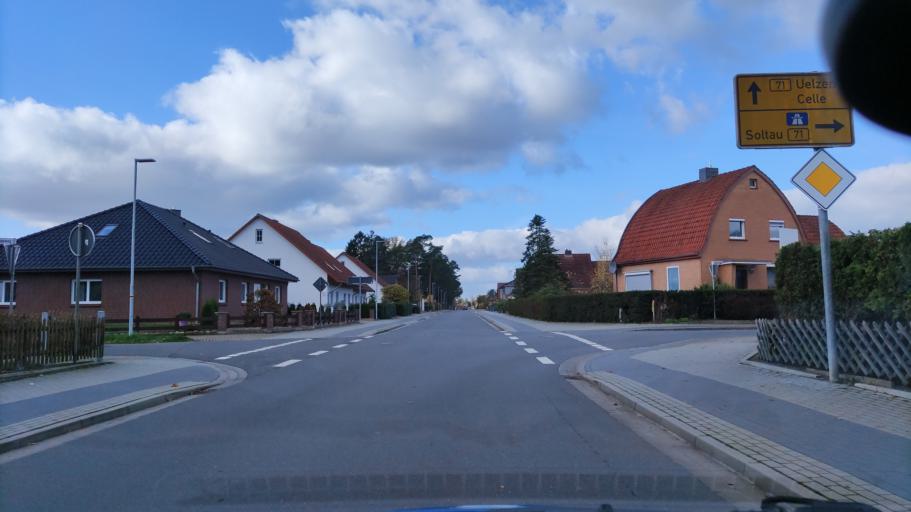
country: DE
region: Lower Saxony
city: Munster
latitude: 52.9856
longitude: 10.1067
